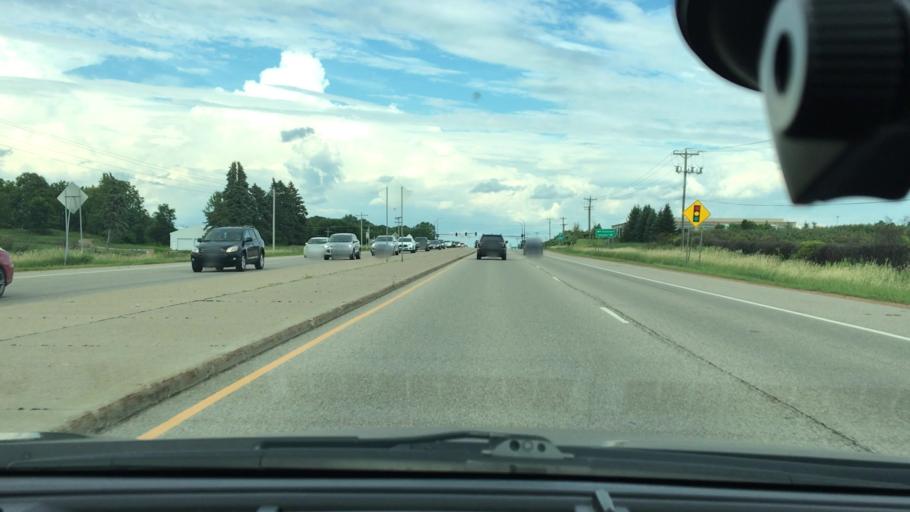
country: US
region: Minnesota
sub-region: Hennepin County
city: Shorewood
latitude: 44.8633
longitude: -93.6016
